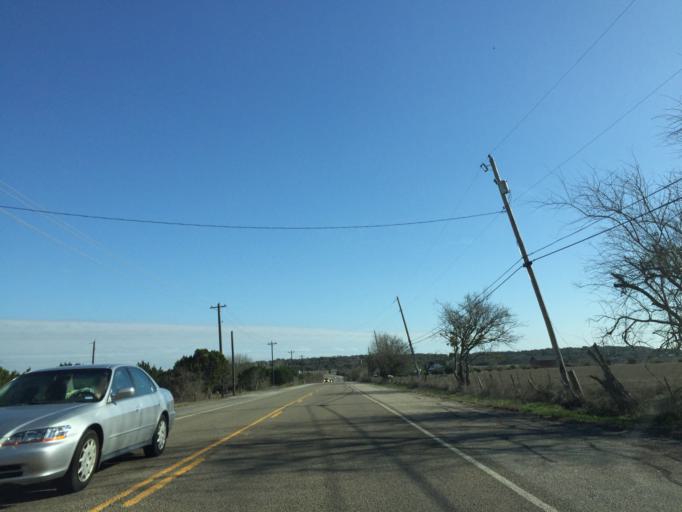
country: US
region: Texas
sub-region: Williamson County
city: Florence
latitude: 30.7720
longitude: -97.8482
